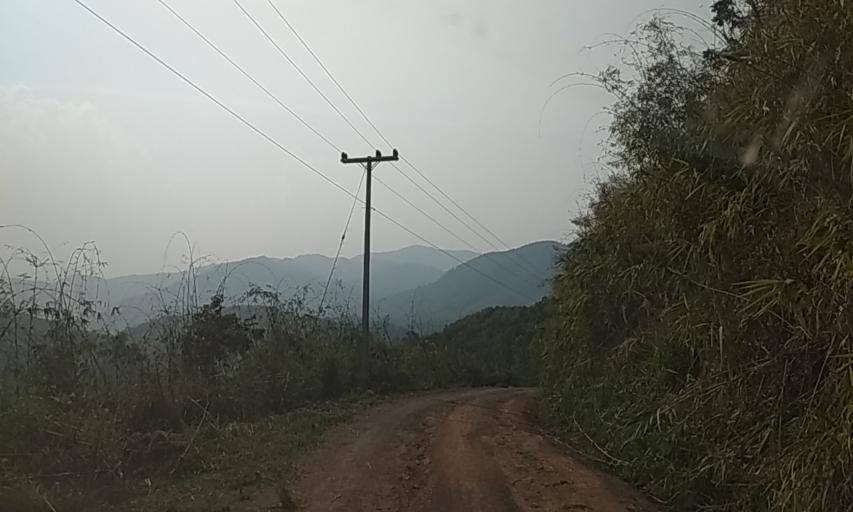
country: LA
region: Louangphabang
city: Louangphabang
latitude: 20.0392
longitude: 101.8197
